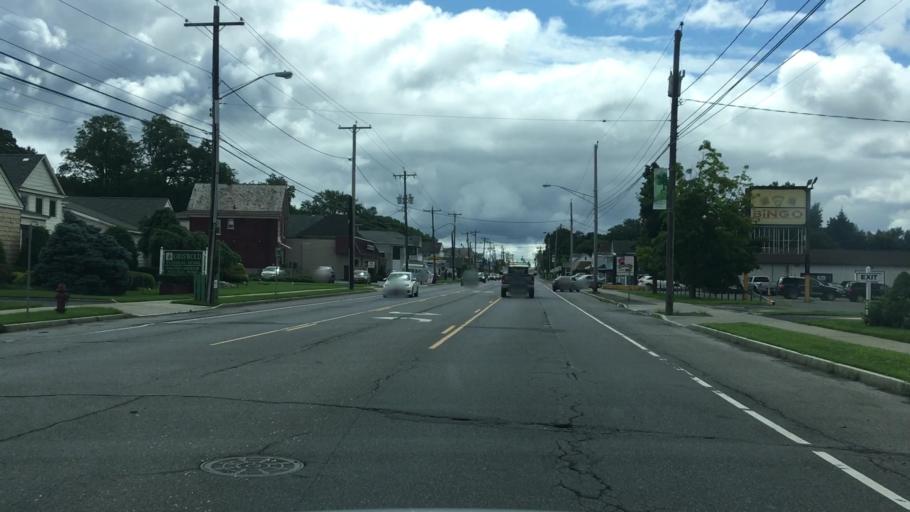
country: US
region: New York
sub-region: Schenectady County
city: Schenectady
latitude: 42.7786
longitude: -73.9021
